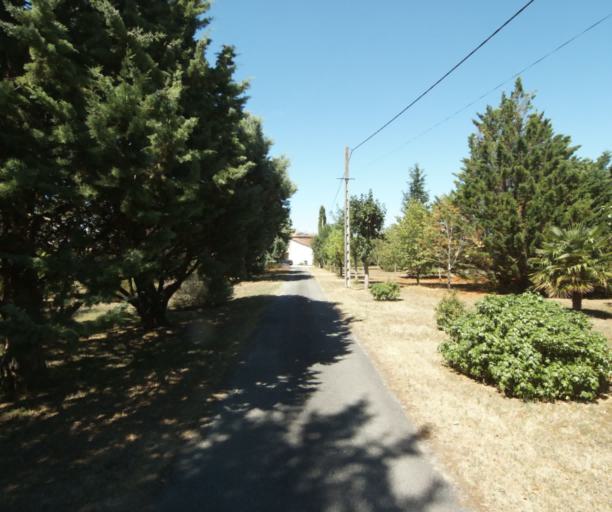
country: FR
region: Midi-Pyrenees
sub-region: Departement de la Haute-Garonne
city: Saint-Felix-Lauragais
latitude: 43.4840
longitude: 1.9161
